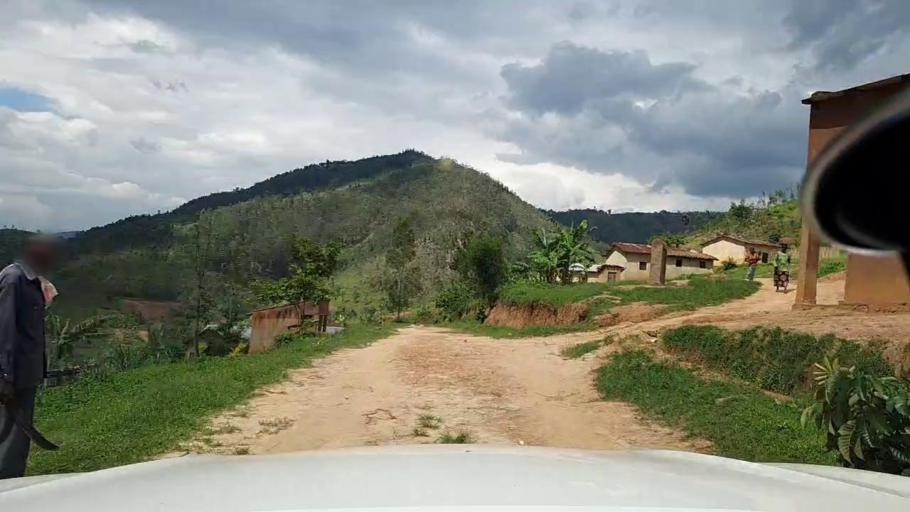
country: RW
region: Southern Province
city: Gitarama
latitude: -1.8189
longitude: 29.8005
